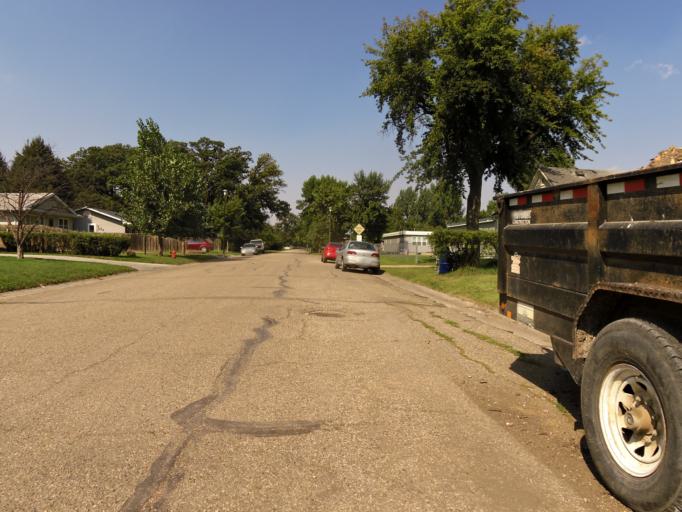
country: US
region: North Dakota
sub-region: Walsh County
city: Grafton
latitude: 48.4217
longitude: -97.4026
